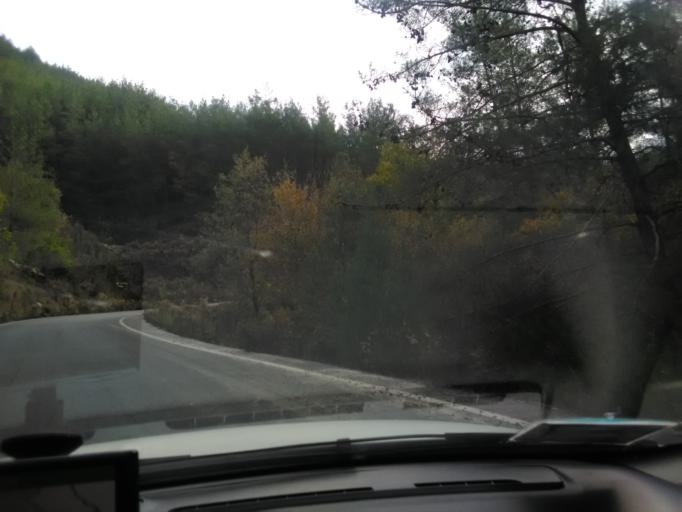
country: TR
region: Antalya
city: Gazipasa
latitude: 36.2405
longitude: 32.4192
